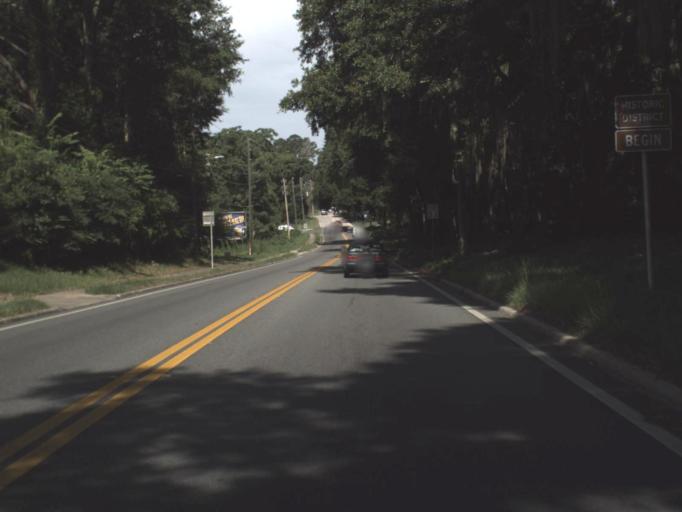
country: US
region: Florida
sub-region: Madison County
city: Madison
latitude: 30.4727
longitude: -83.4075
